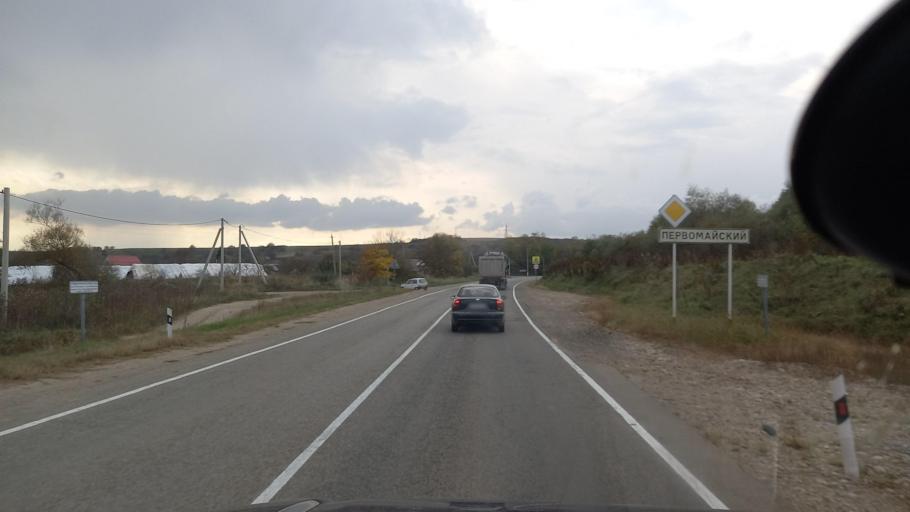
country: RU
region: Krasnodarskiy
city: Mostovskoy
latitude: 44.3893
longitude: 40.7427
